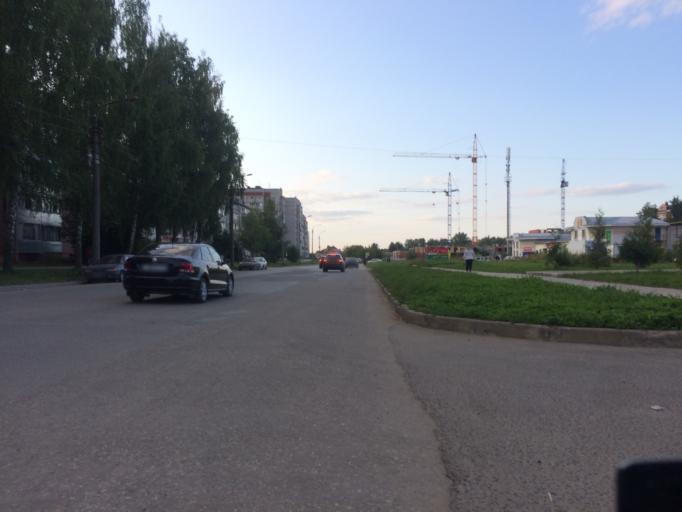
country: RU
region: Mariy-El
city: Medvedevo
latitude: 56.6429
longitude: 47.8449
